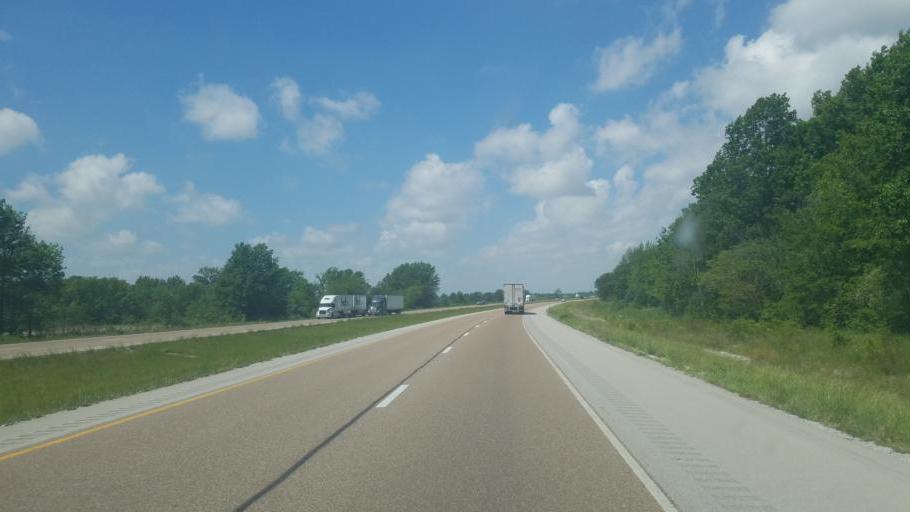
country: US
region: Illinois
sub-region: Cumberland County
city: Greenup
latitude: 39.2752
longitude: -88.0905
